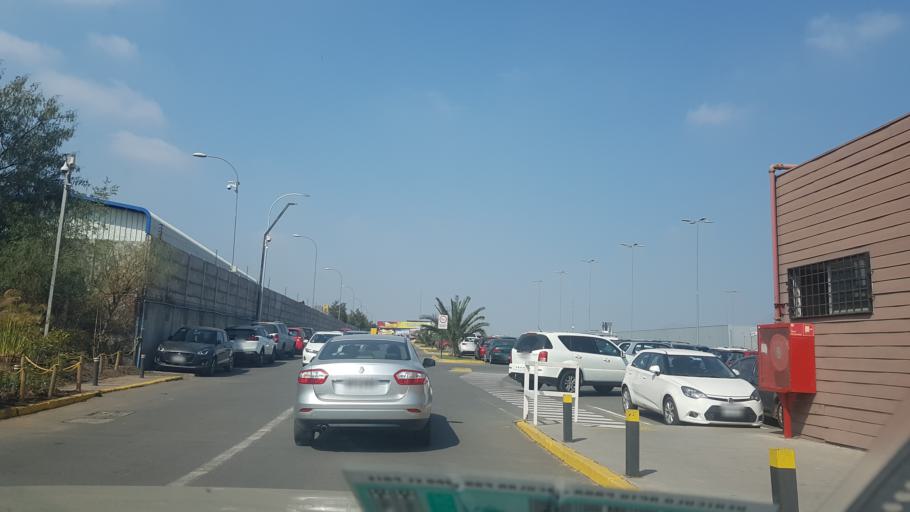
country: CL
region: Santiago Metropolitan
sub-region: Provincia de Chacabuco
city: Chicureo Abajo
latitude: -33.3322
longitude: -70.7032
